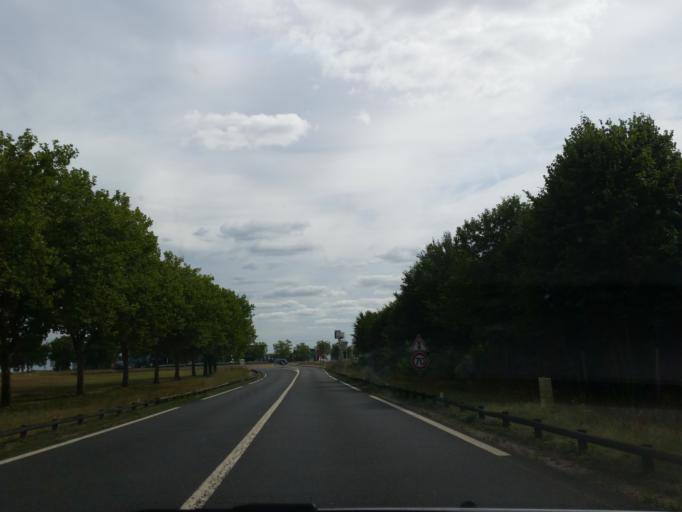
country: FR
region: Centre
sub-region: Departement du Loir-et-Cher
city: La Chaussee-Saint-Victor
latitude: 47.6195
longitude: 1.3466
